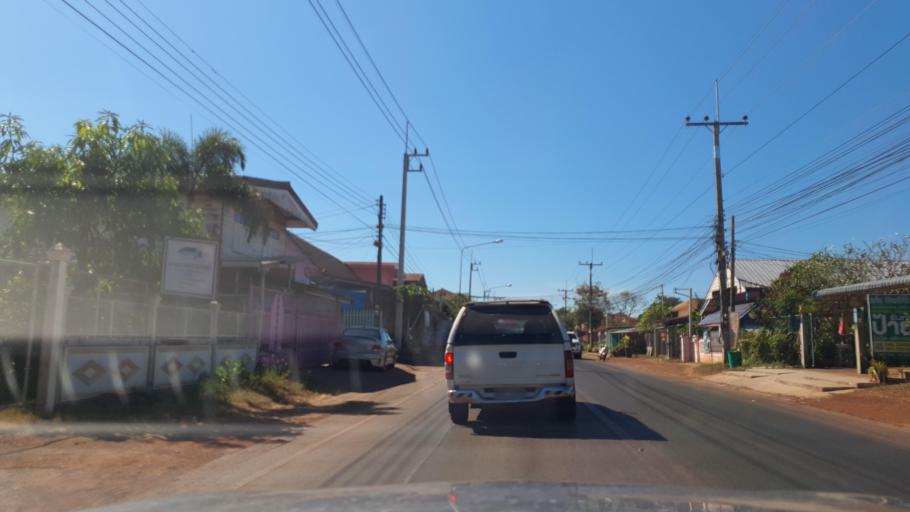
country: TH
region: Sakon Nakhon
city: Phon Na Kaeo
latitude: 17.2612
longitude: 104.1901
